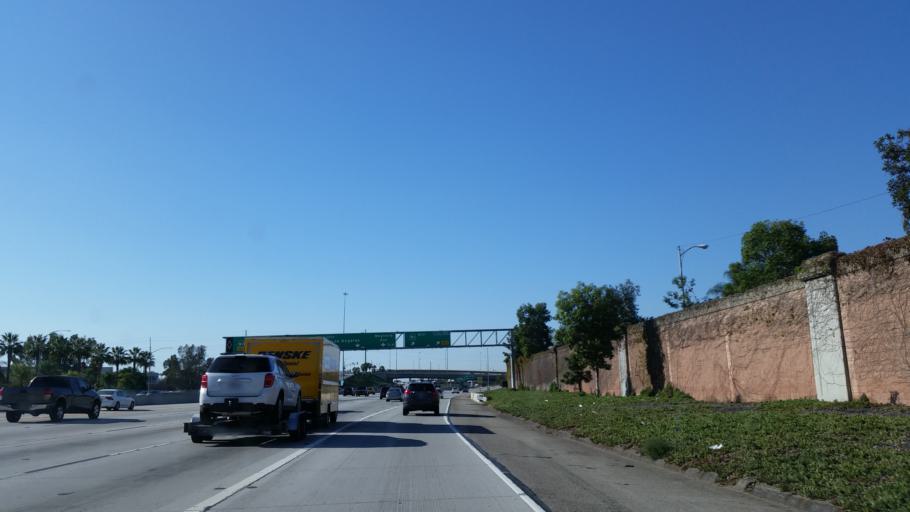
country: US
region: California
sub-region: Orange County
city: Buena Park
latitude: 33.8520
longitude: -117.9711
